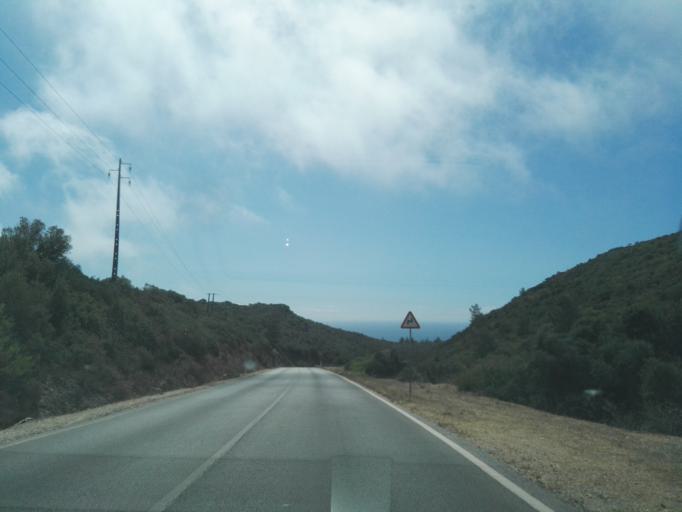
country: PT
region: Setubal
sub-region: Sesimbra
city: Sesimbra
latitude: 38.4447
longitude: -9.0867
